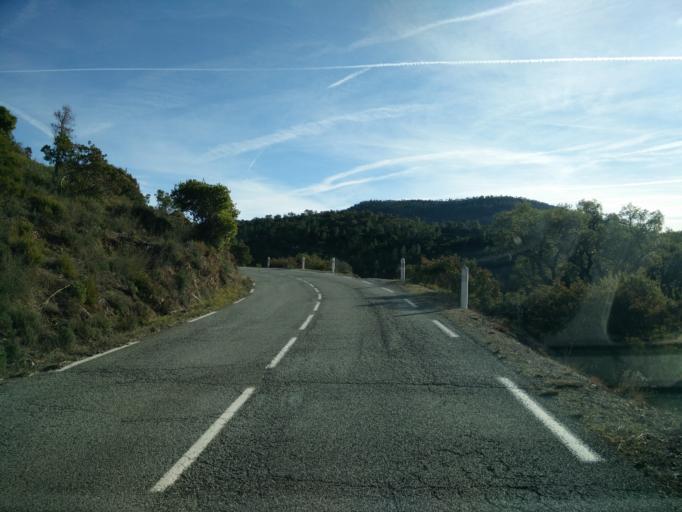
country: FR
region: Provence-Alpes-Cote d'Azur
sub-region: Departement du Var
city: Saint-Raphael
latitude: 43.5009
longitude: 6.7822
